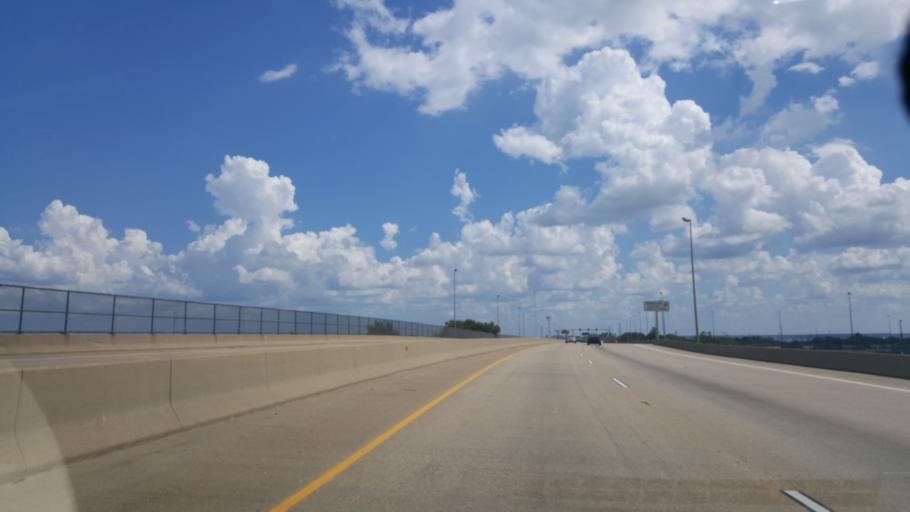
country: US
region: Virginia
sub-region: City of Newport News
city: Newport News
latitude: 36.9744
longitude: -76.4205
